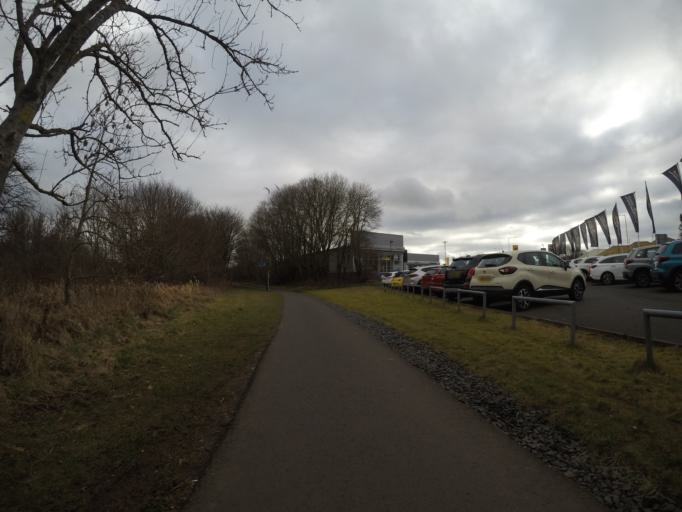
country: GB
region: Scotland
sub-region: North Ayrshire
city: Irvine
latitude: 55.6088
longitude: -4.6372
